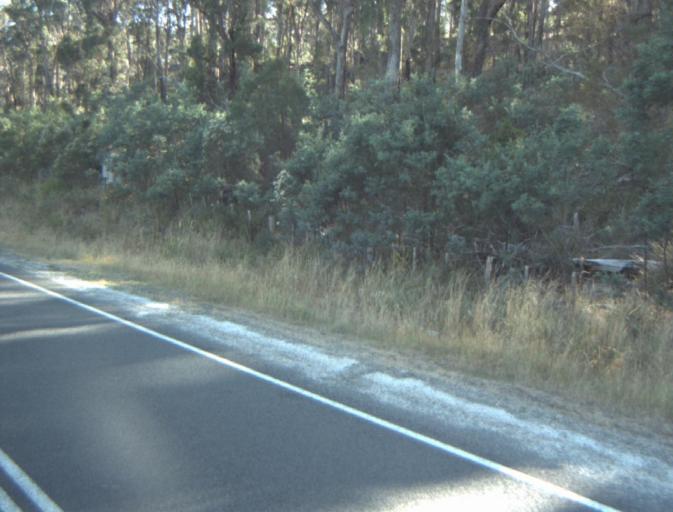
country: AU
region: Tasmania
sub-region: Launceston
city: Newstead
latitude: -41.4258
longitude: 147.2551
